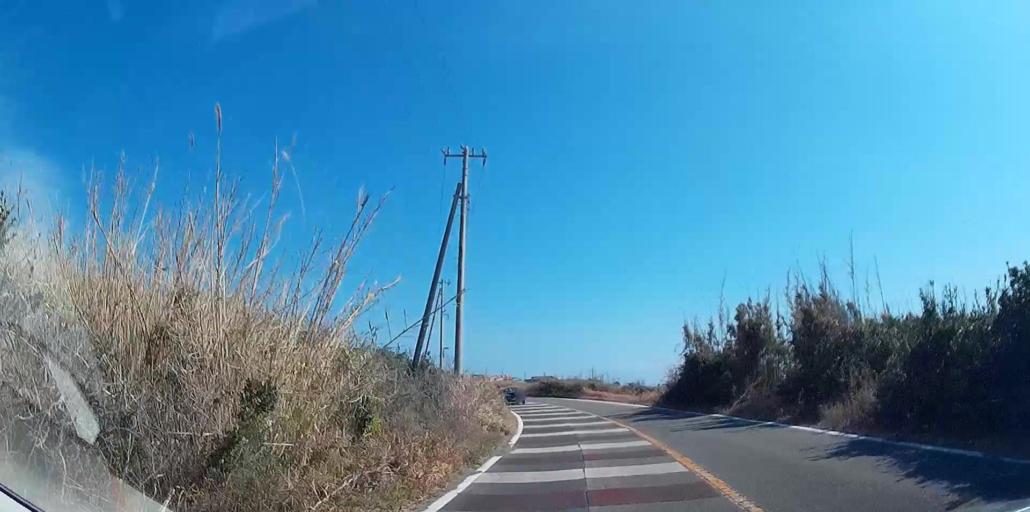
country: JP
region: Chiba
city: Tateyama
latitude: 34.9077
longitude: 139.8659
